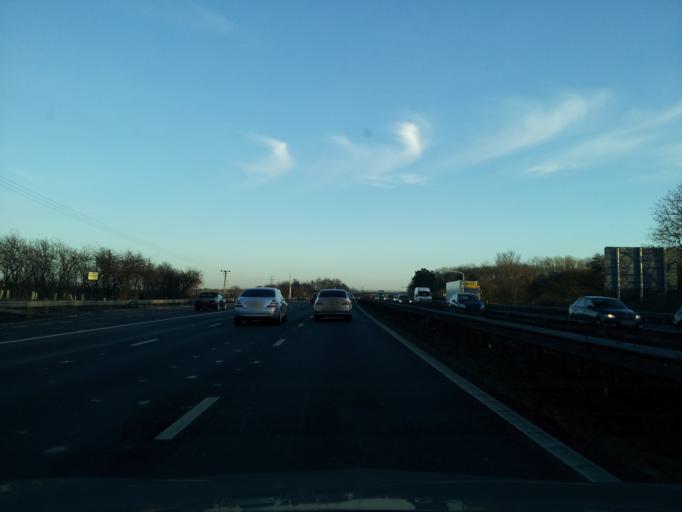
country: GB
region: England
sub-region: Central Bedfordshire
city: Ridgmont
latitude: 52.0149
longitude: -0.5605
